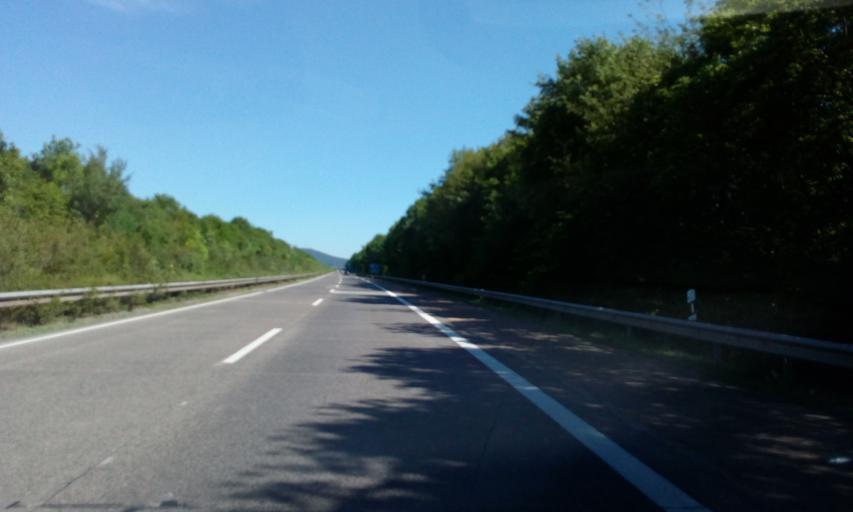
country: DE
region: Rheinland-Pfalz
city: Rivenich
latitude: 49.8896
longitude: 6.8514
